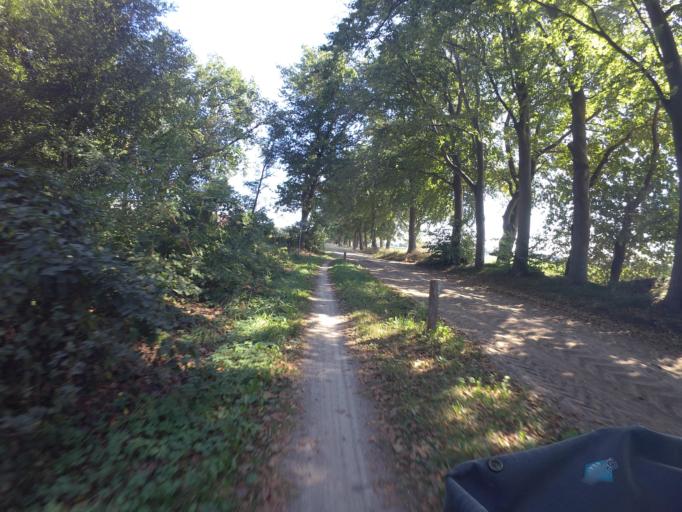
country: NL
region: Overijssel
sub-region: Gemeente Dalfsen
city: Dalfsen
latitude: 52.4714
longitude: 6.2913
